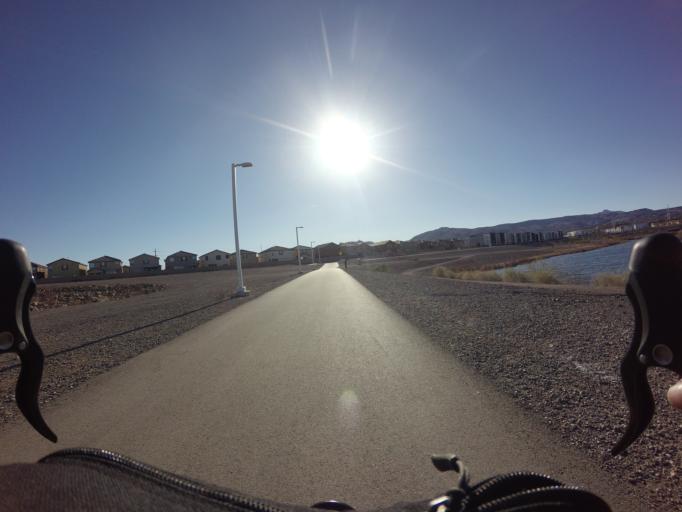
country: US
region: Nevada
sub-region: Clark County
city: Whitney
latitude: 36.0389
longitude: -115.0513
